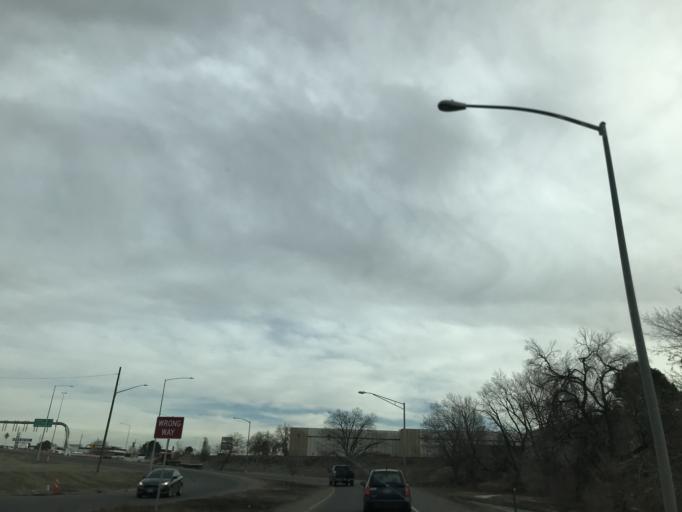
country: US
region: Colorado
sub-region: Adams County
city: Aurora
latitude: 39.7743
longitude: -104.8648
